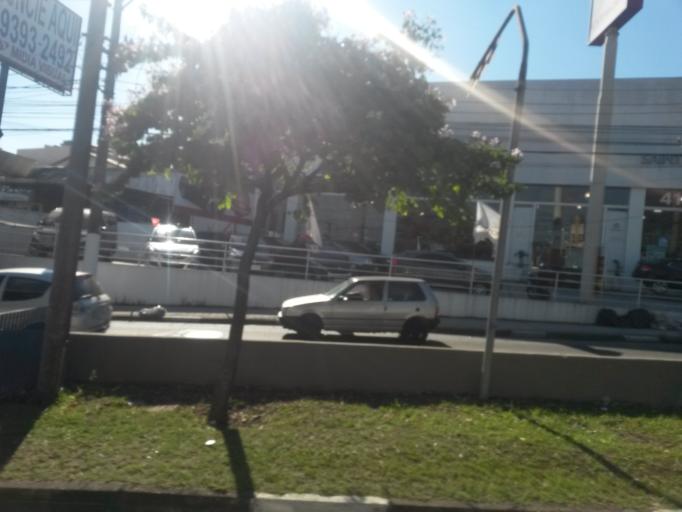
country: BR
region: Sao Paulo
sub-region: Santo Andre
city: Santo Andre
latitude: -23.6828
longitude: -46.5444
